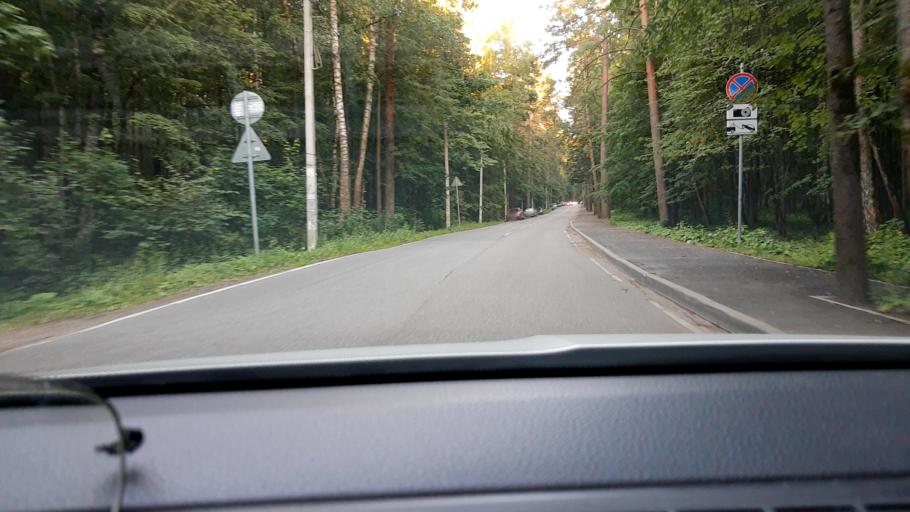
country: RU
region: Moskovskaya
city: Arkhangel'skoye
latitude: 55.7919
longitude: 37.2749
